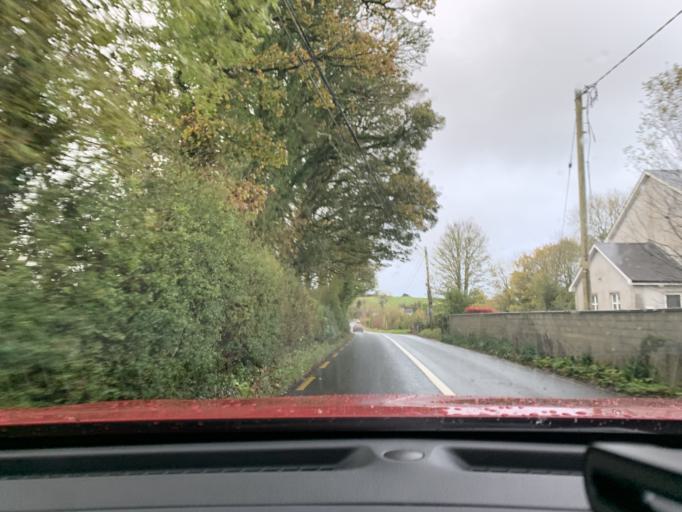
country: IE
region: Connaught
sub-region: Sligo
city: Ballymote
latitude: 54.0601
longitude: -8.5094
